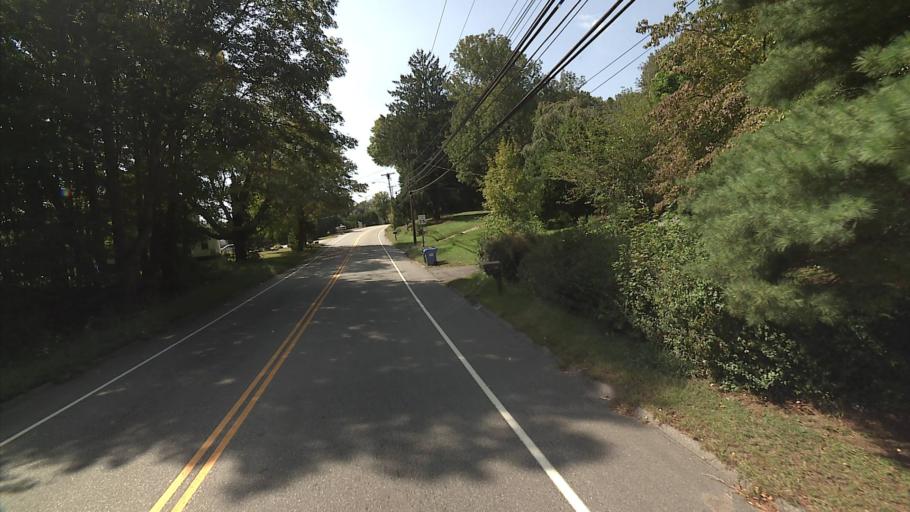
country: US
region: Connecticut
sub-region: New London County
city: Norwich
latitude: 41.5599
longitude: -72.0697
